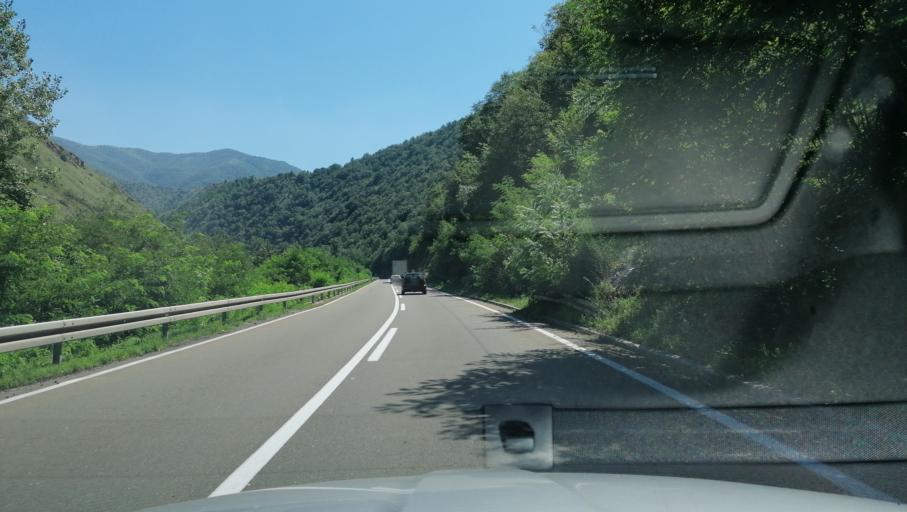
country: RS
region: Central Serbia
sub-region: Raski Okrug
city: Kraljevo
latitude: 43.5645
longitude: 20.6033
